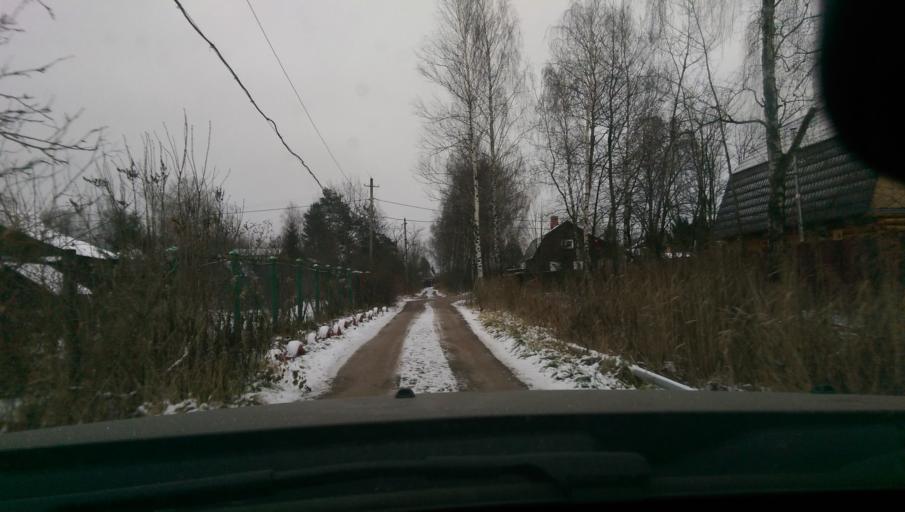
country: RU
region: Moskovskaya
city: Imeni Vorovskogo
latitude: 55.7339
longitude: 38.2856
